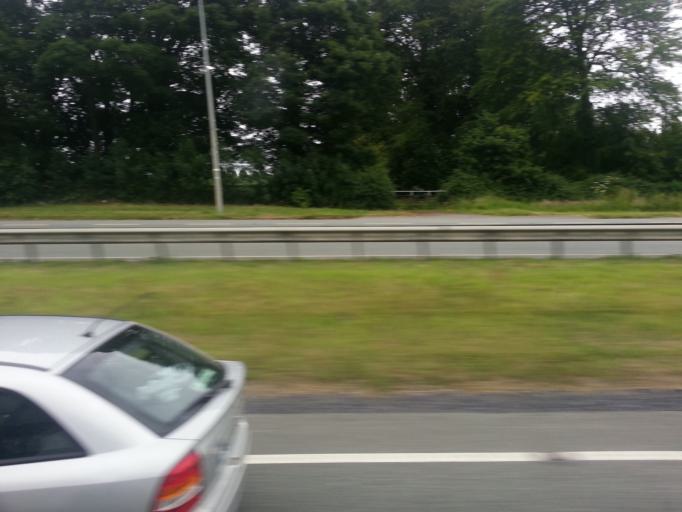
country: IE
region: Leinster
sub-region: South Dublin
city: Newcastle
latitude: 53.2637
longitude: -6.5329
